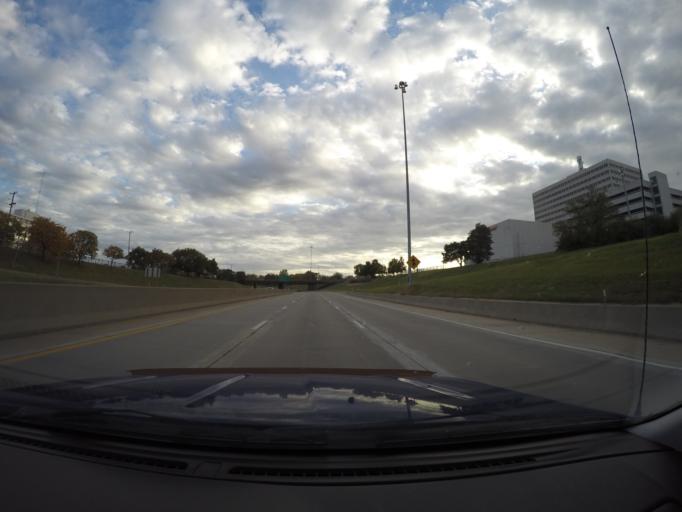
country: US
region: Kansas
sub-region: Shawnee County
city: Topeka
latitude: 39.0467
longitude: -95.6714
